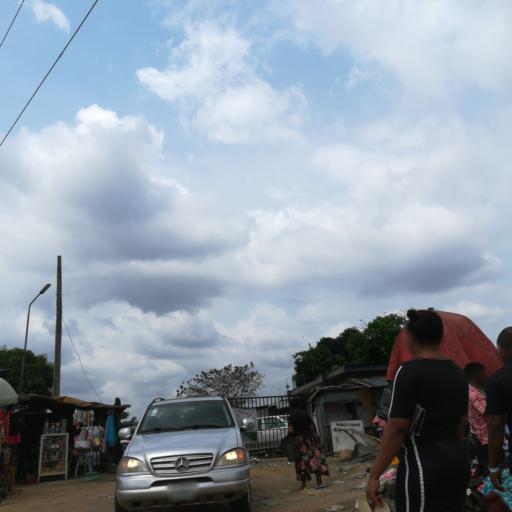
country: NG
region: Rivers
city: Port Harcourt
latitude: 4.8523
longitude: 7.0633
